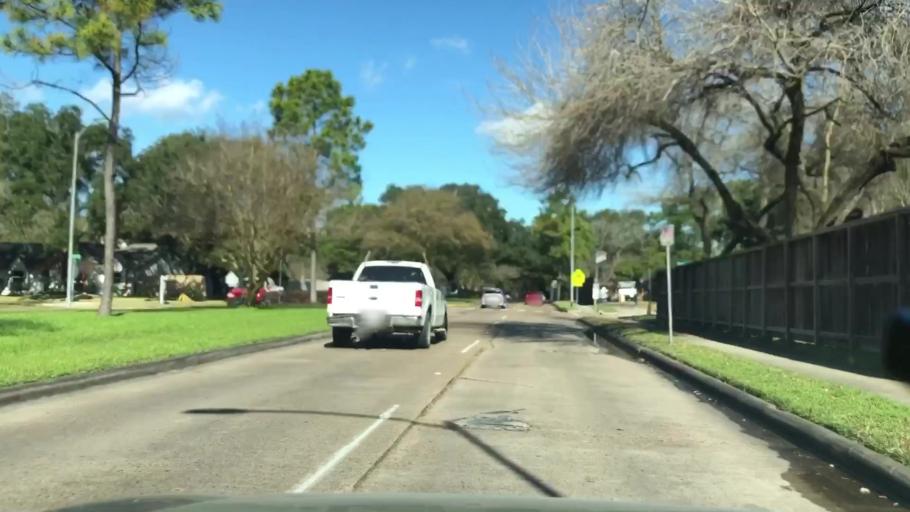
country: US
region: Texas
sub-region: Harris County
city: Bellaire
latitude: 29.6698
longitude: -95.4922
